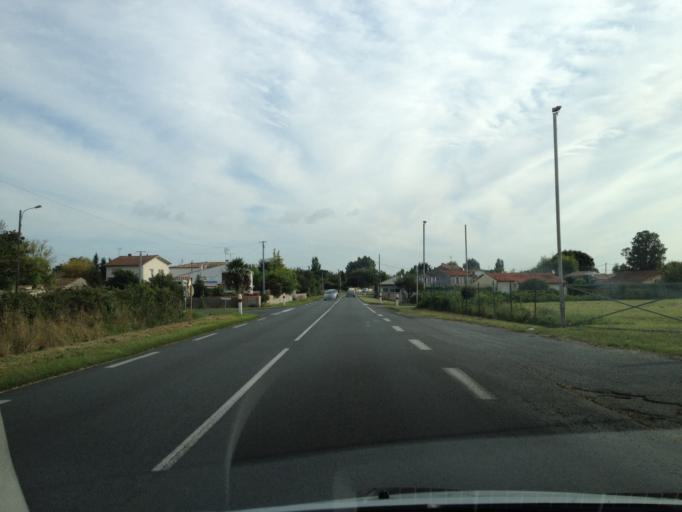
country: FR
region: Poitou-Charentes
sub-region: Departement de la Charente-Maritime
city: Le Gua
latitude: 45.7255
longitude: -0.9633
